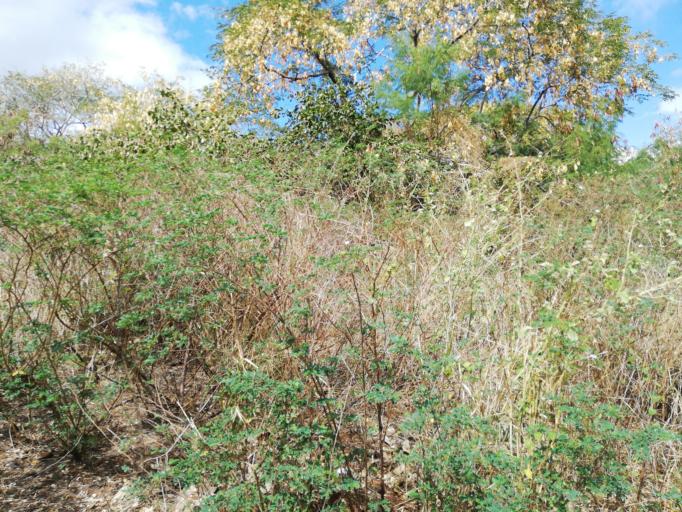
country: MU
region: Black River
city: Petite Riviere
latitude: -20.1931
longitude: 57.4665
